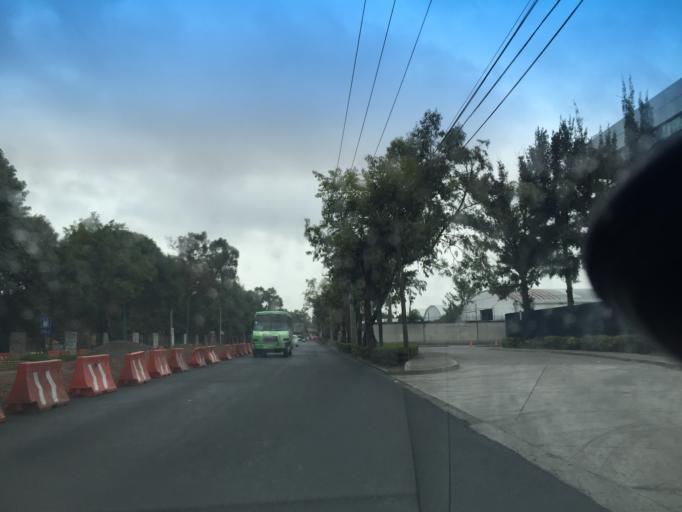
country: MX
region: Mexico City
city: Azcapotzalco
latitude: 19.5030
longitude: -99.1800
